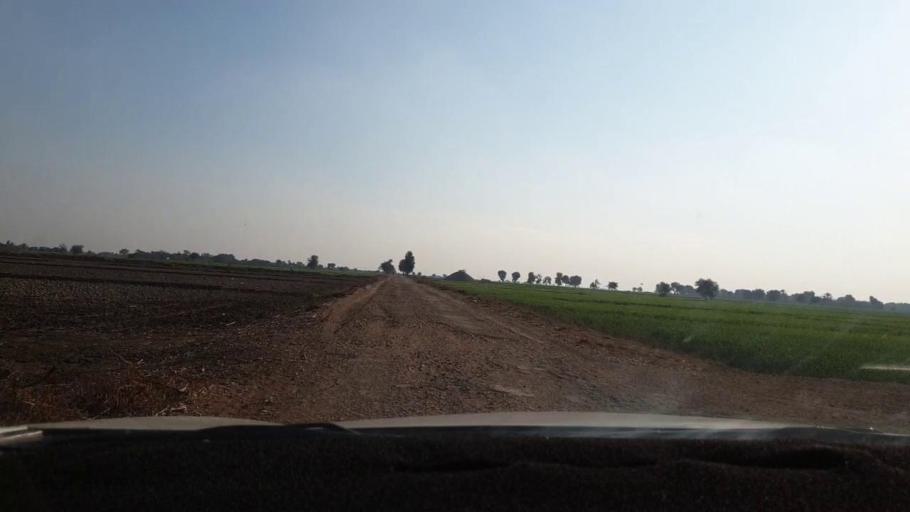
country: PK
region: Sindh
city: Berani
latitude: 25.7707
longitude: 68.7686
